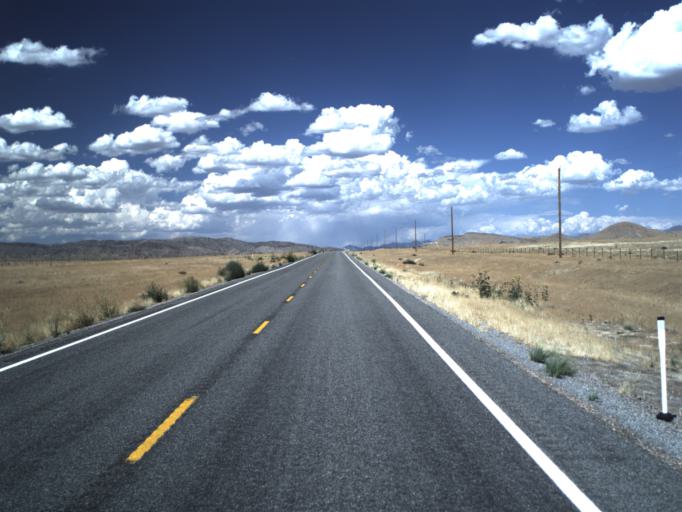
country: US
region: Utah
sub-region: Millard County
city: Delta
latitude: 39.6080
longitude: -112.3212
